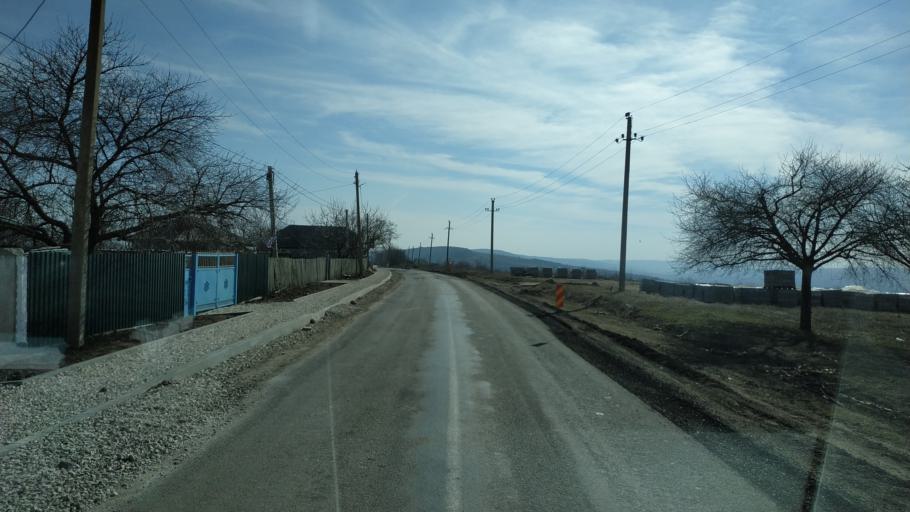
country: MD
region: Nisporeni
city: Nisporeni
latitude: 47.2042
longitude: 28.0597
